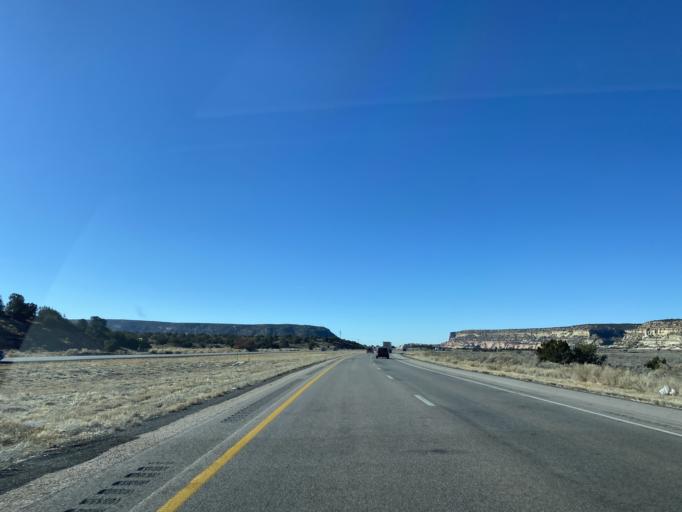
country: US
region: Arizona
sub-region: Apache County
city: Houck
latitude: 35.3851
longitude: -109.0140
